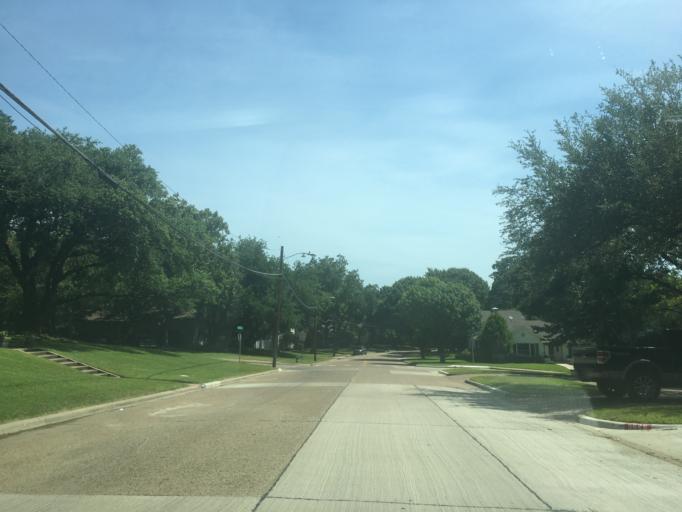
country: US
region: Texas
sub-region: Dallas County
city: Highland Park
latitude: 32.8685
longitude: -96.7202
